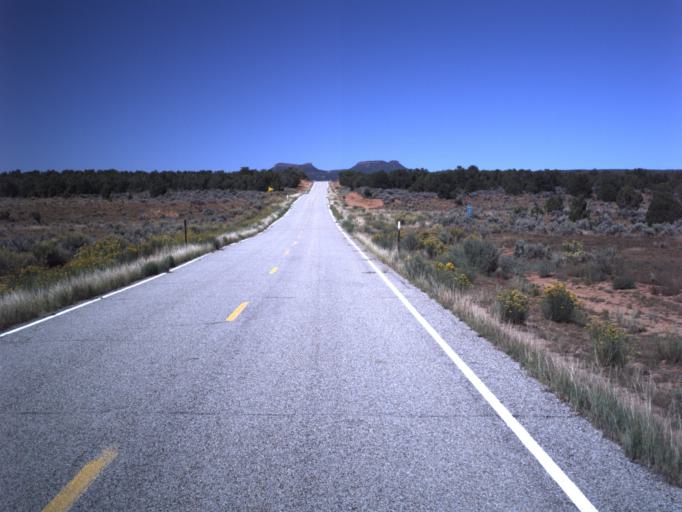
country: US
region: Utah
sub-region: San Juan County
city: Blanding
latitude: 37.4984
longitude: -109.8952
